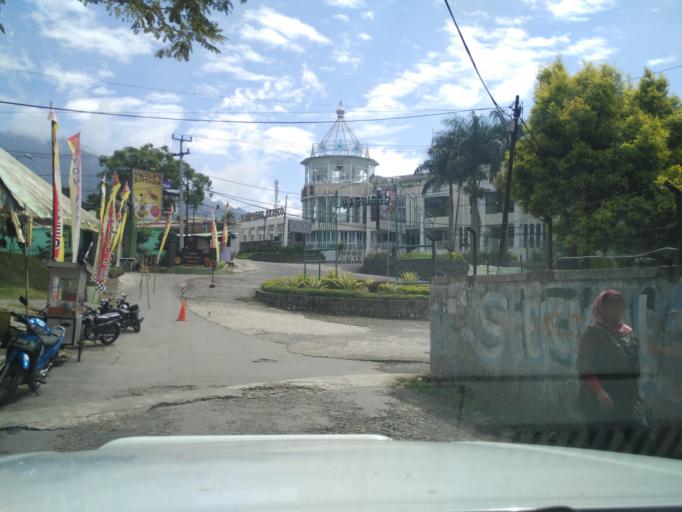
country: ID
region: West Java
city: Caringin
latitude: -6.7154
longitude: 107.0239
